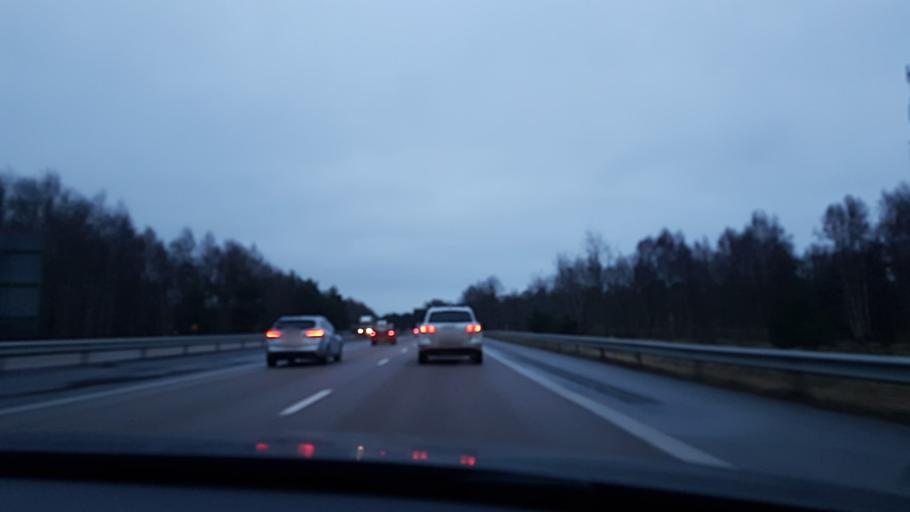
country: SE
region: Skane
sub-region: Kavlinge Kommun
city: Loddekopinge
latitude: 55.7612
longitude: 12.9919
